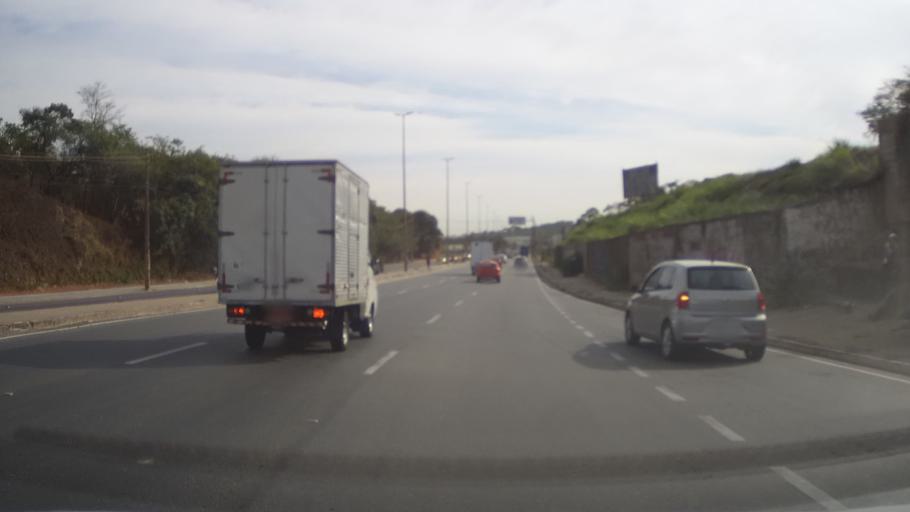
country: BR
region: Minas Gerais
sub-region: Contagem
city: Contagem
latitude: -19.9151
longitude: -44.0540
